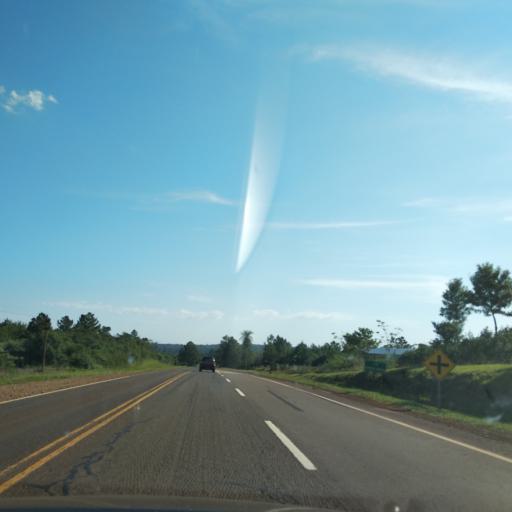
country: AR
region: Misiones
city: Gobernador Roca
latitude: -27.1657
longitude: -55.4399
